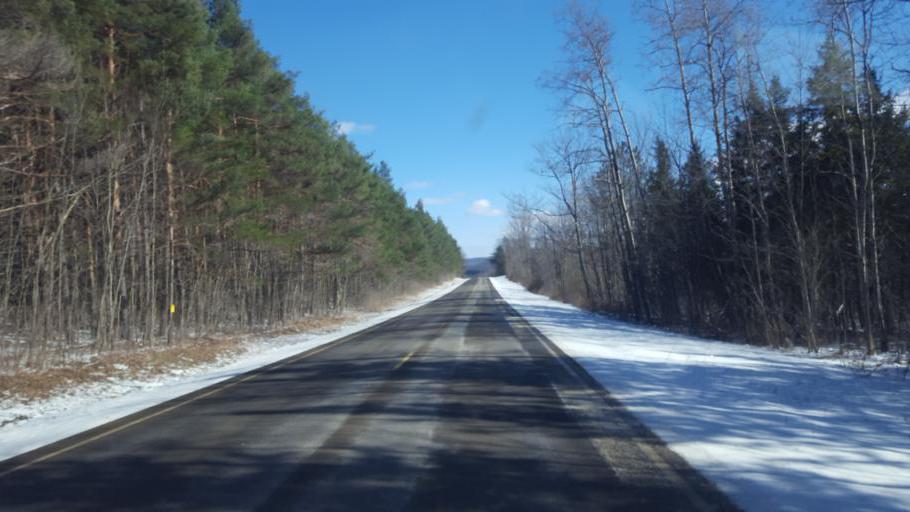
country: US
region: New York
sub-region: Allegany County
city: Friendship
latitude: 42.1825
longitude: -78.0808
